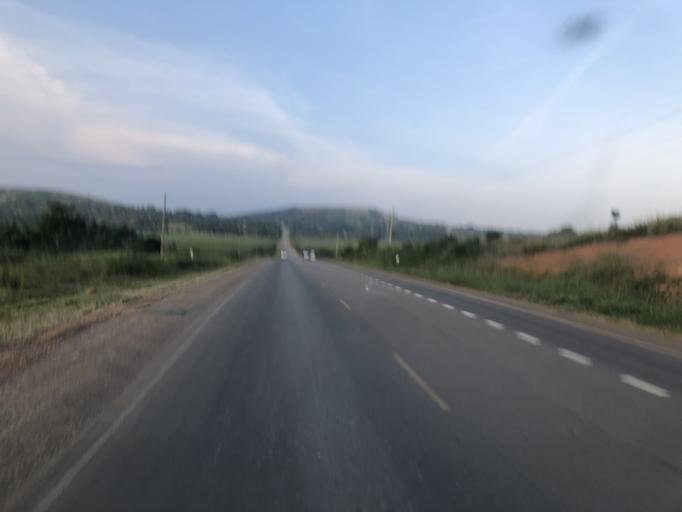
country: UG
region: Central Region
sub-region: Mpigi District
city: Mpigi
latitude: 0.1809
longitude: 32.2815
